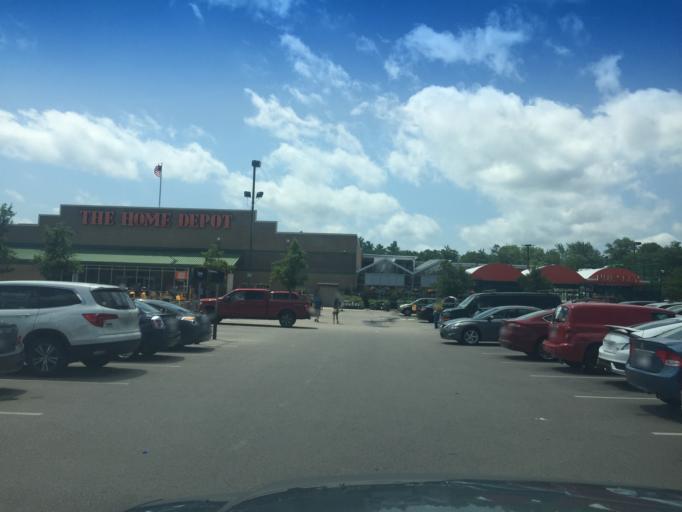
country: US
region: Massachusetts
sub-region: Norfolk County
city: Bellingham
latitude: 42.1124
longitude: -71.4692
